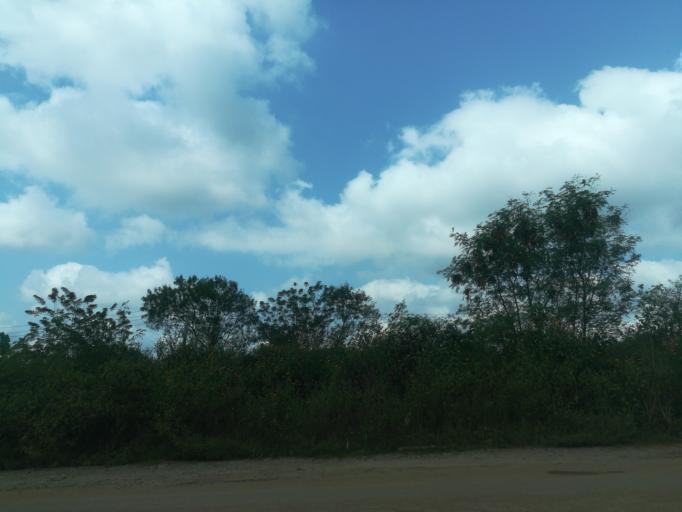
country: NG
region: Oyo
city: Moniya
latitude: 7.5690
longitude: 3.9146
